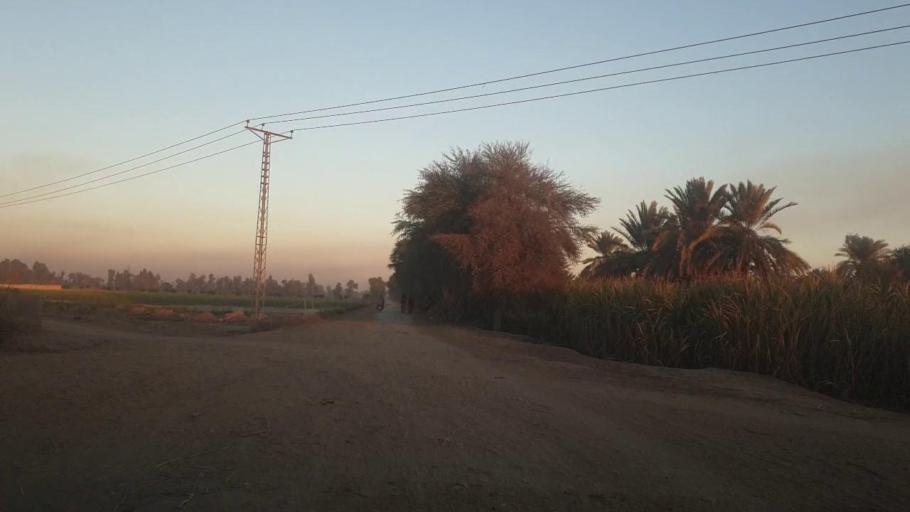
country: PK
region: Sindh
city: Ghotki
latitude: 28.0387
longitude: 69.3181
